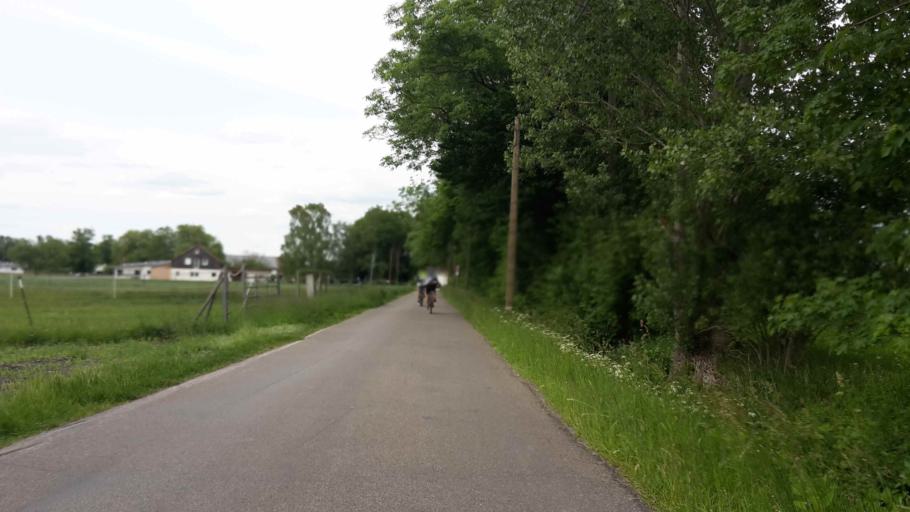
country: DE
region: Bavaria
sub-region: Upper Bavaria
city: Karlsfeld
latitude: 48.2185
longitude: 11.4353
